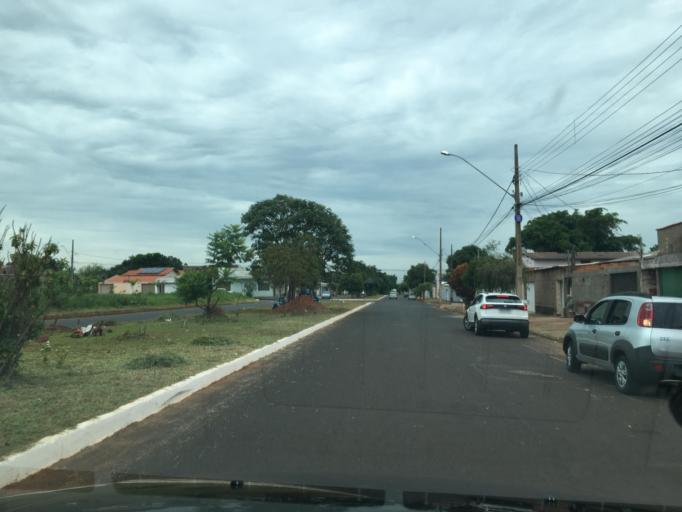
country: BR
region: Minas Gerais
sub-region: Uberlandia
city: Uberlandia
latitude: -18.8787
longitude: -48.2275
